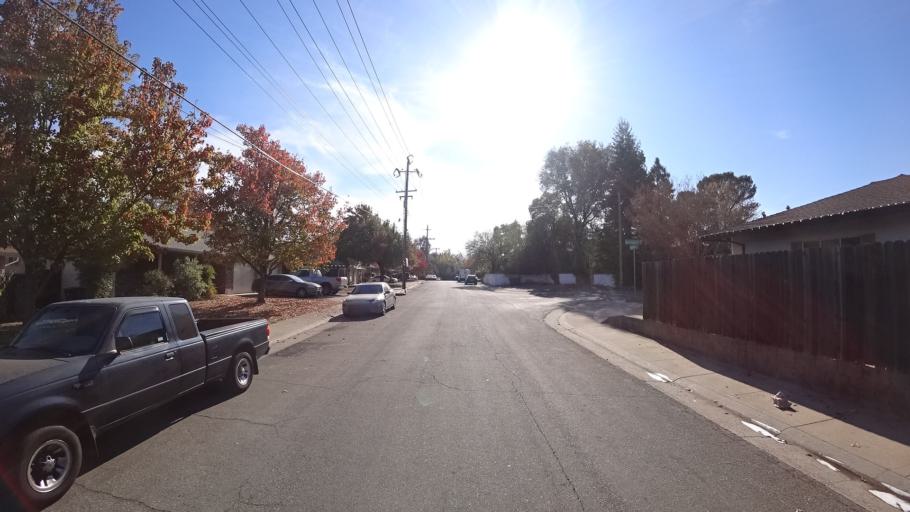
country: US
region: California
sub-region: Sacramento County
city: Fair Oaks
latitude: 38.6653
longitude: -121.2890
